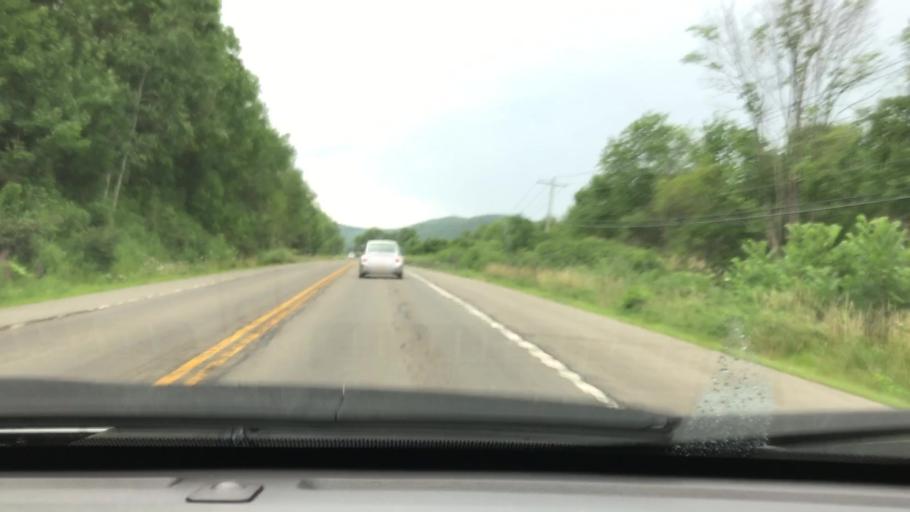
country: US
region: New York
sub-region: Cattaraugus County
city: Salamanca
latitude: 42.2353
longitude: -78.6391
